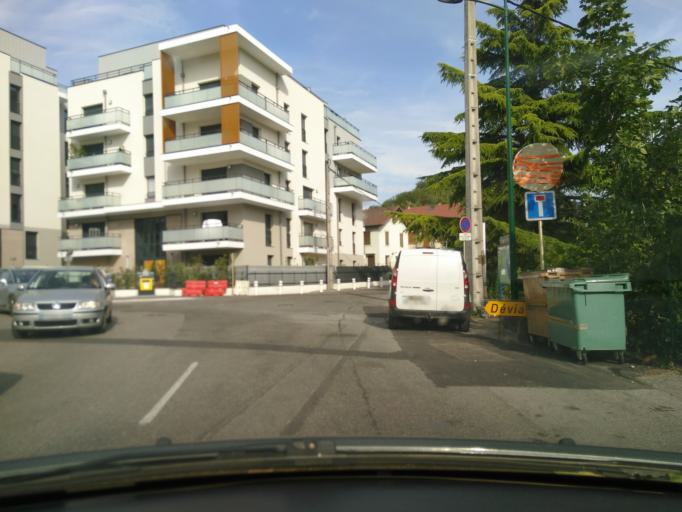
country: FR
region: Rhone-Alpes
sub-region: Departement de la Haute-Savoie
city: Saint-Julien-en-Genevois
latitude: 46.1409
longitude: 6.0850
